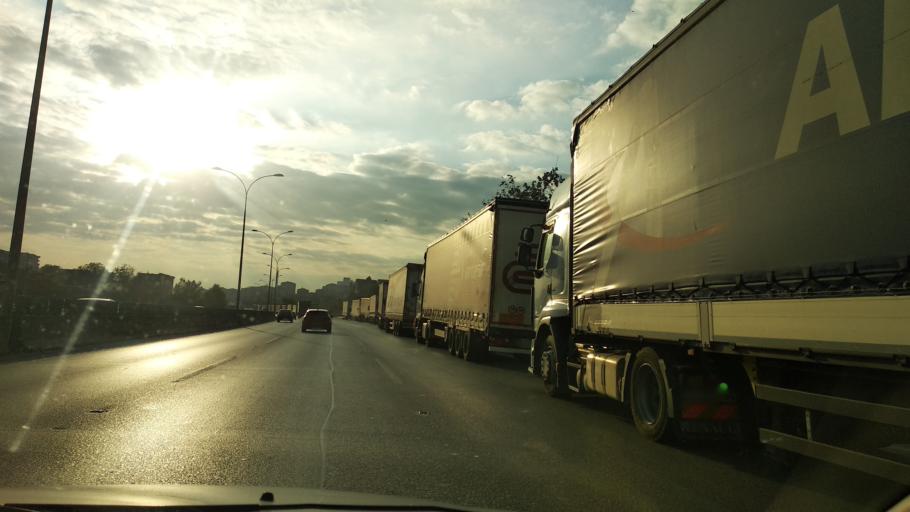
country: TR
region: Istanbul
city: Pendik
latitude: 40.8740
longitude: 29.2941
